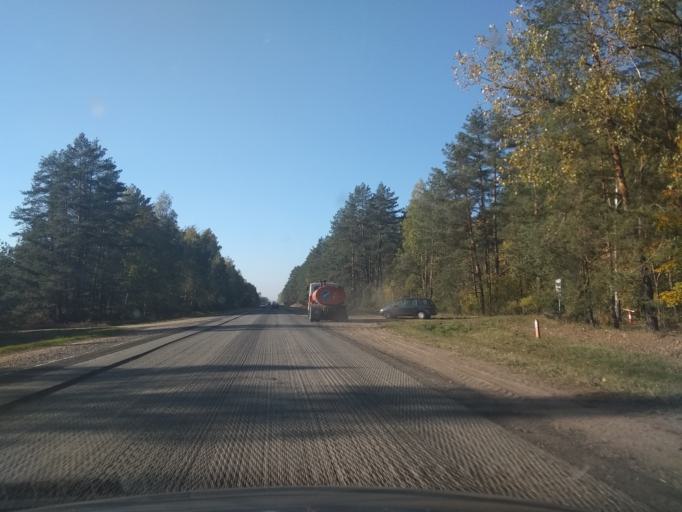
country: BY
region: Grodnenskaya
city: Zhyrovichy
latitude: 53.0606
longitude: 25.4282
